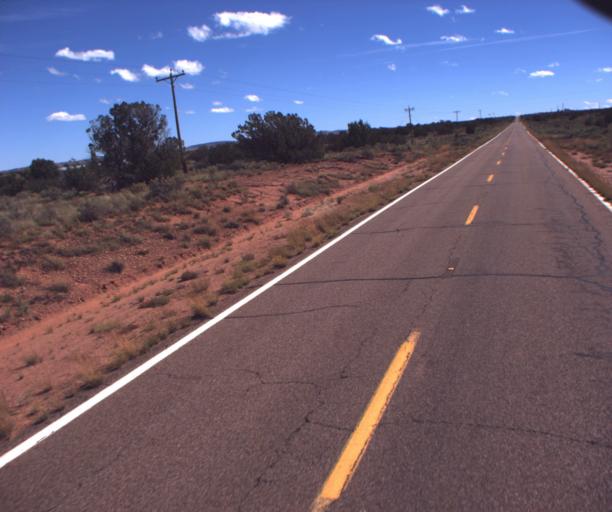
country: US
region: Arizona
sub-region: Apache County
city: Saint Johns
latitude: 34.6060
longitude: -109.6553
